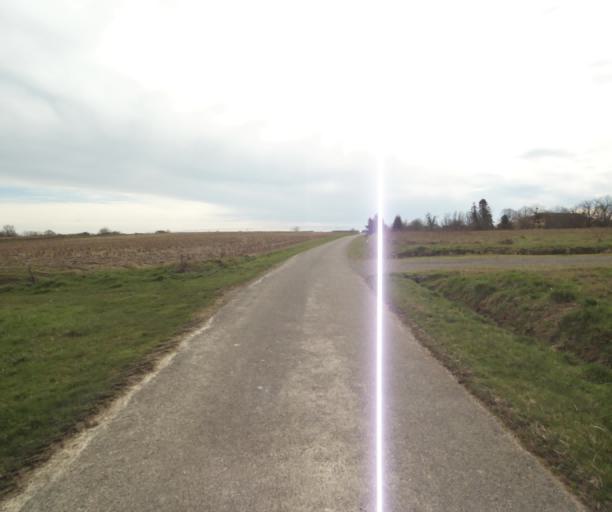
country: FR
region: Aquitaine
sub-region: Departement des Landes
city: Gabarret
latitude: 43.9232
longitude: 0.0440
